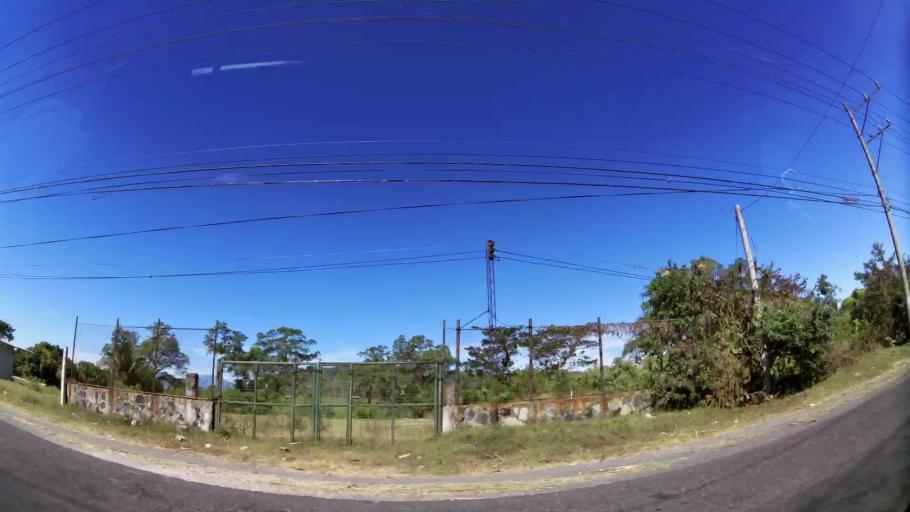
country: SV
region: La Libertad
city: San Juan Opico
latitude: 13.8098
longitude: -89.3577
